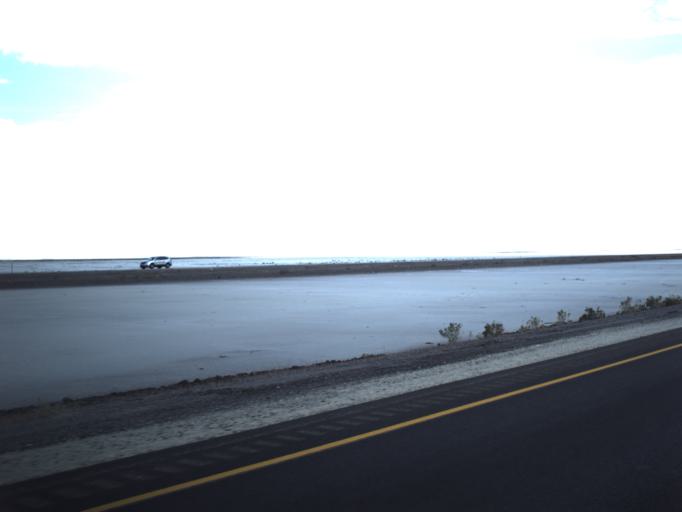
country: US
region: Utah
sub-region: Tooele County
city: Wendover
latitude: 40.7316
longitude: -113.5310
